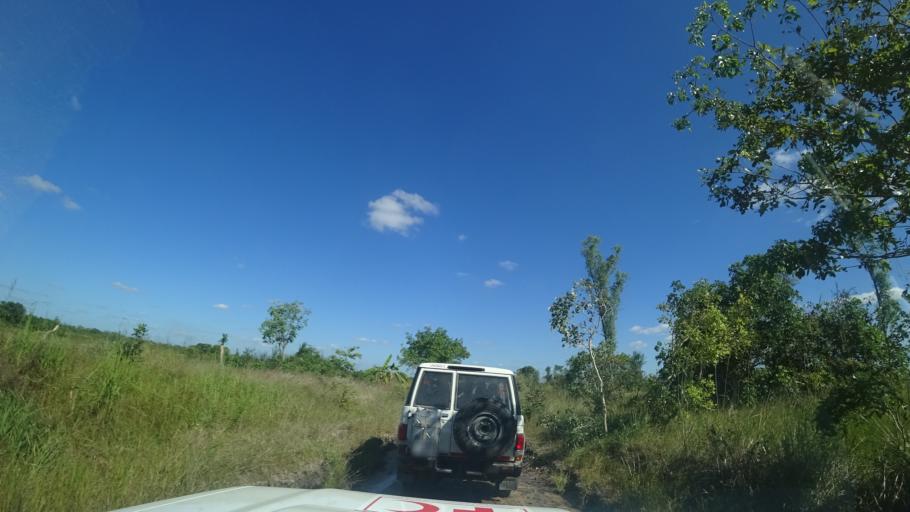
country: MZ
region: Sofala
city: Dondo
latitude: -19.4753
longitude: 34.6298
